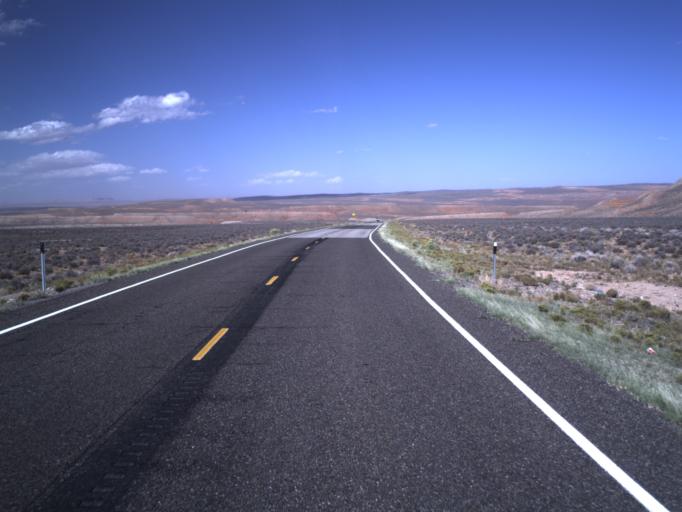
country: US
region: Utah
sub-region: Wayne County
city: Loa
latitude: 38.1219
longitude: -110.6202
